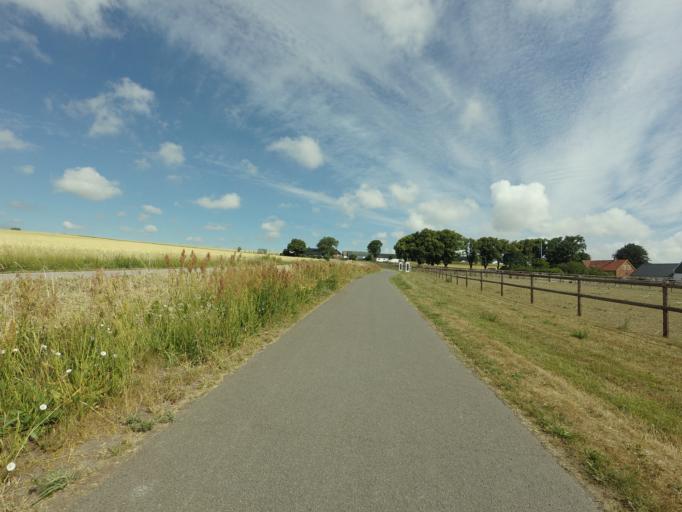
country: SE
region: Skane
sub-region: Simrishamns Kommun
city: Simrishamn
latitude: 55.4826
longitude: 14.2847
